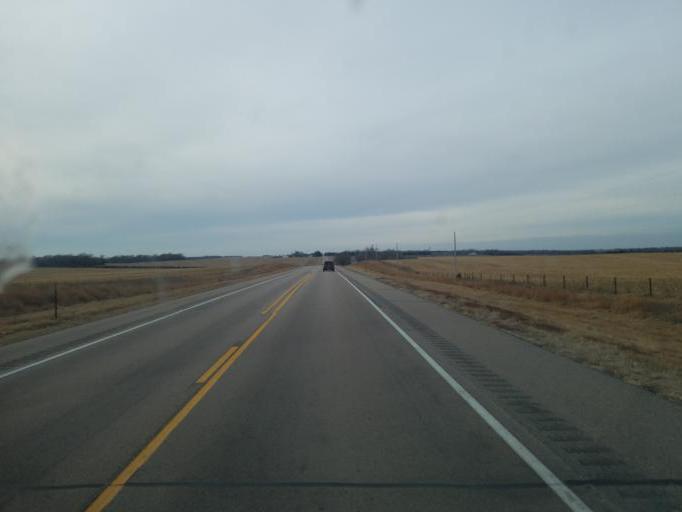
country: US
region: Nebraska
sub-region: Antelope County
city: Neligh
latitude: 42.3353
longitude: -98.2046
